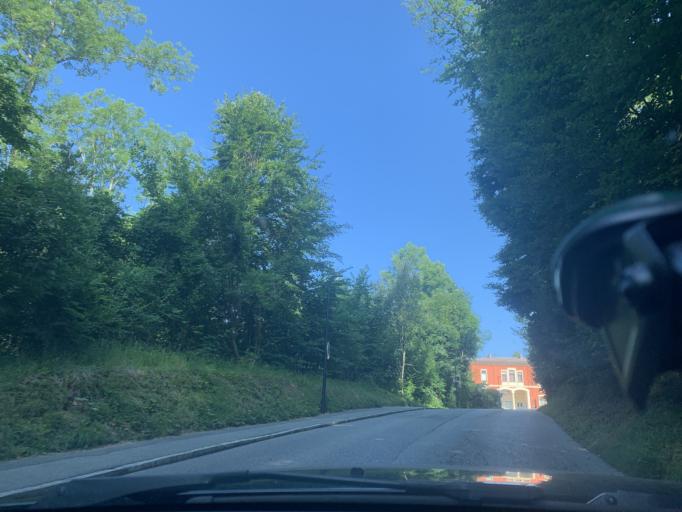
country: DE
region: Bavaria
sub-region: Upper Bavaria
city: Pocking
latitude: 47.9608
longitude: 11.3079
